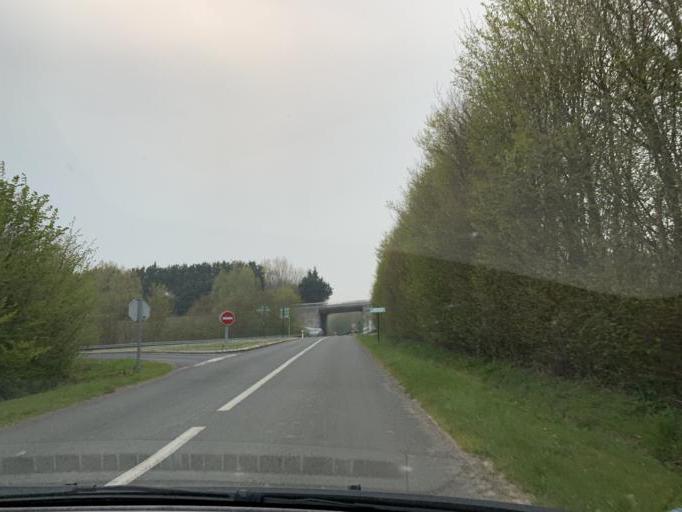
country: FR
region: Nord-Pas-de-Calais
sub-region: Departement du Pas-de-Calais
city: Wimille
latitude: 50.7639
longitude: 1.6392
